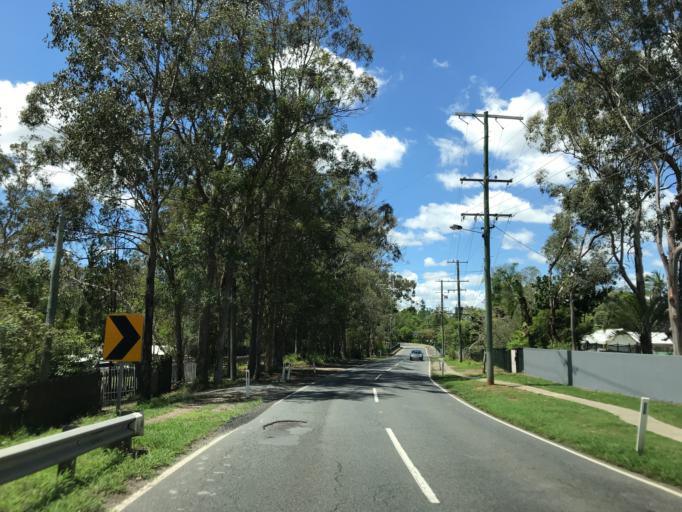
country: AU
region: Queensland
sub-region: Brisbane
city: Kenmore Hills
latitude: -27.5233
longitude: 152.9462
